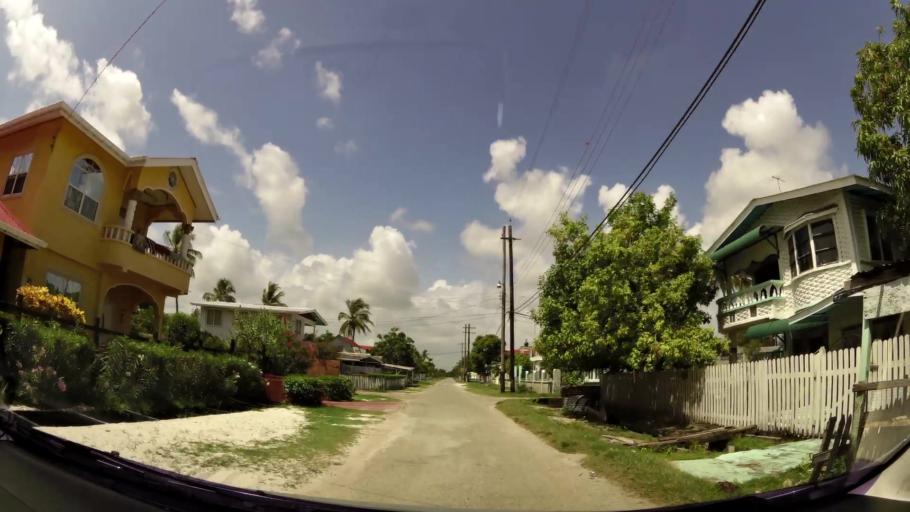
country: GY
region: Demerara-Mahaica
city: Mahaica Village
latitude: 6.7650
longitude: -58.0103
